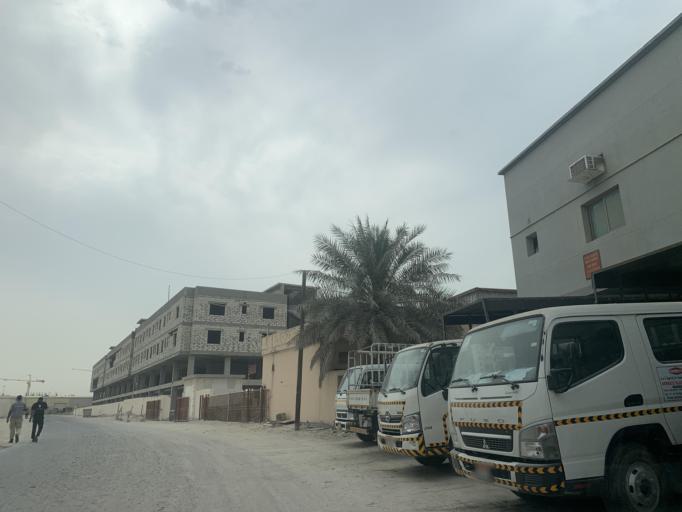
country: BH
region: Northern
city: Madinat `Isa
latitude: 26.1783
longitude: 50.5094
